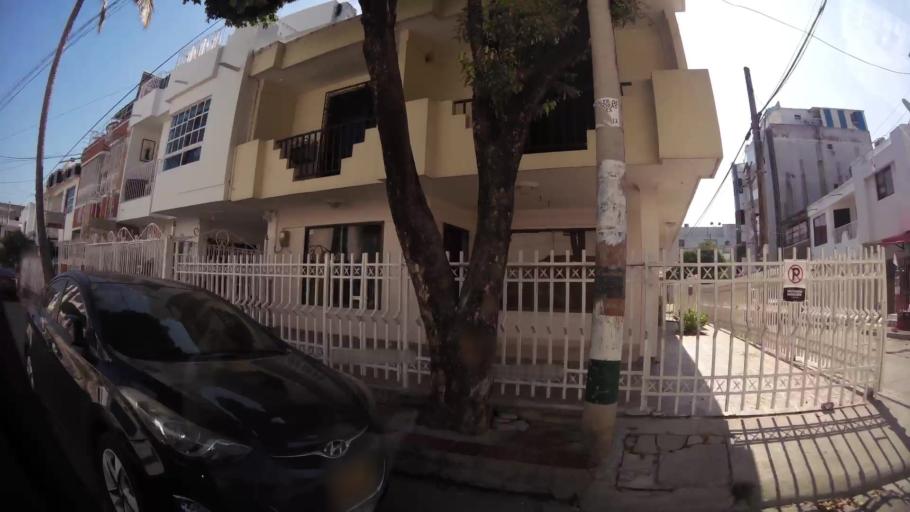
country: CO
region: Bolivar
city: Cartagena
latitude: 10.3859
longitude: -75.4687
